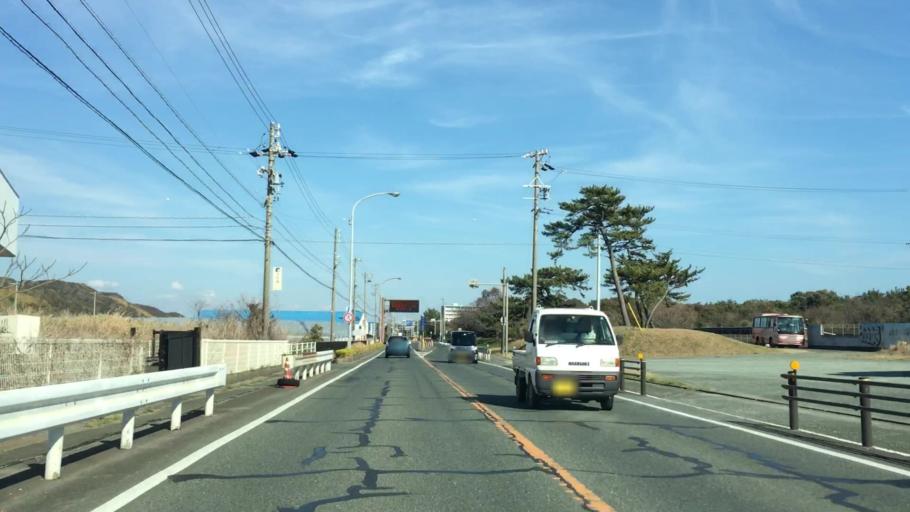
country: JP
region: Shizuoka
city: Kosai-shi
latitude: 34.6803
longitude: 137.5298
